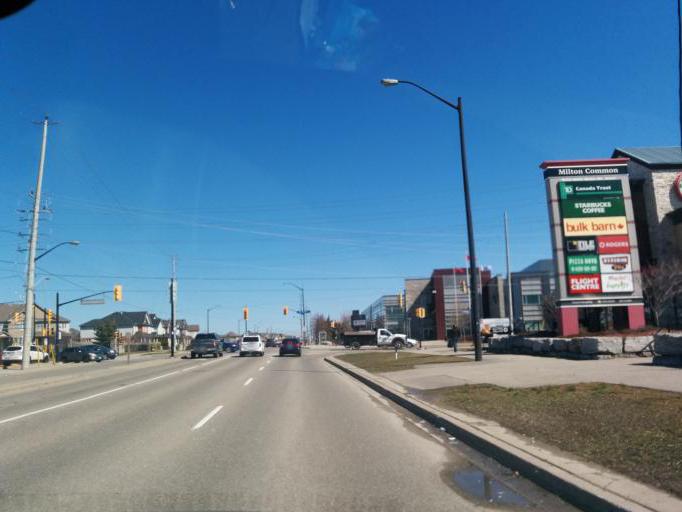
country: CA
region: Ontario
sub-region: Halton
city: Milton
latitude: 43.5276
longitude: -79.8674
